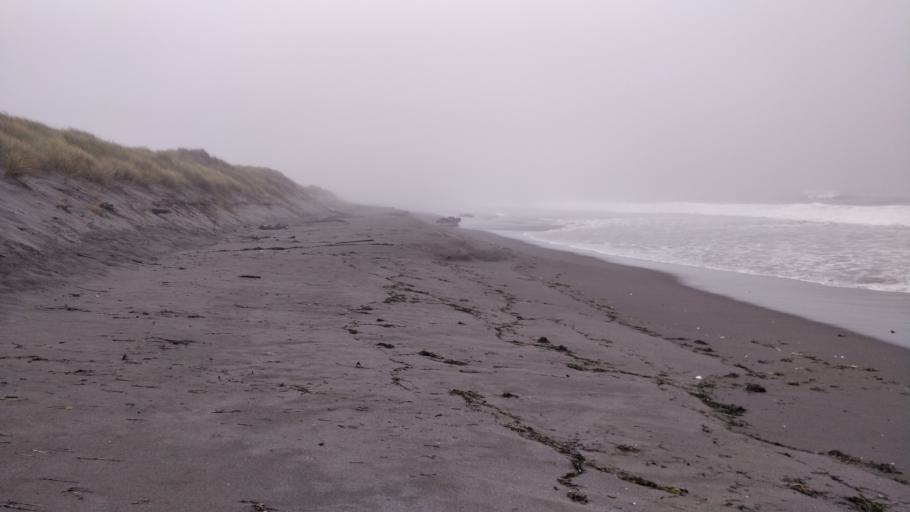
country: US
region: California
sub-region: Humboldt County
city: Bayview
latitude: 40.7984
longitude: -124.2059
